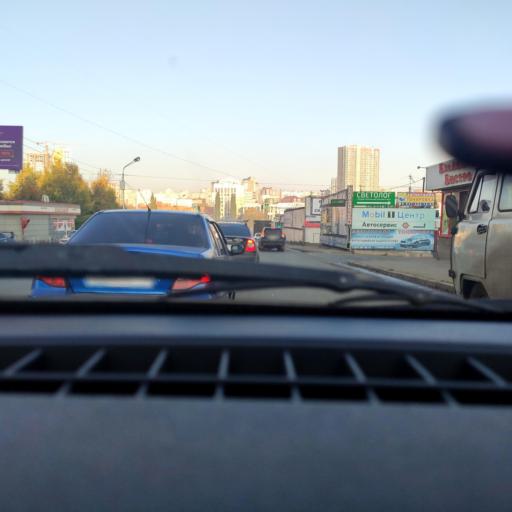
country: RU
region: Bashkortostan
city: Ufa
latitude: 54.7233
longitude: 55.9935
